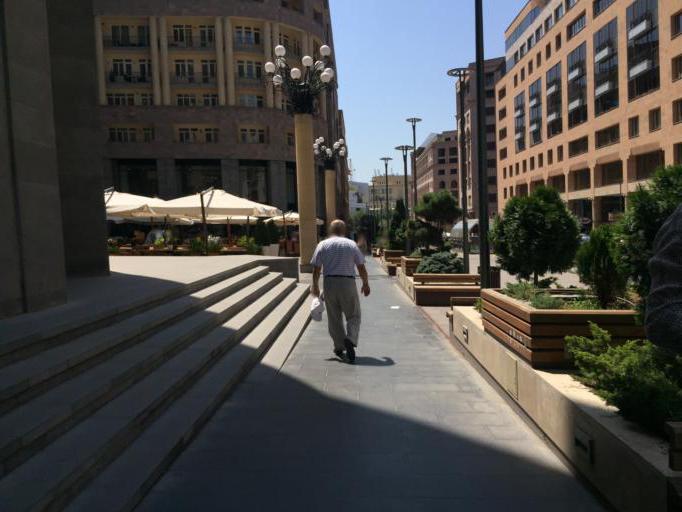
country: AM
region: Yerevan
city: Yerevan
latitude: 40.1824
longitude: 44.5148
